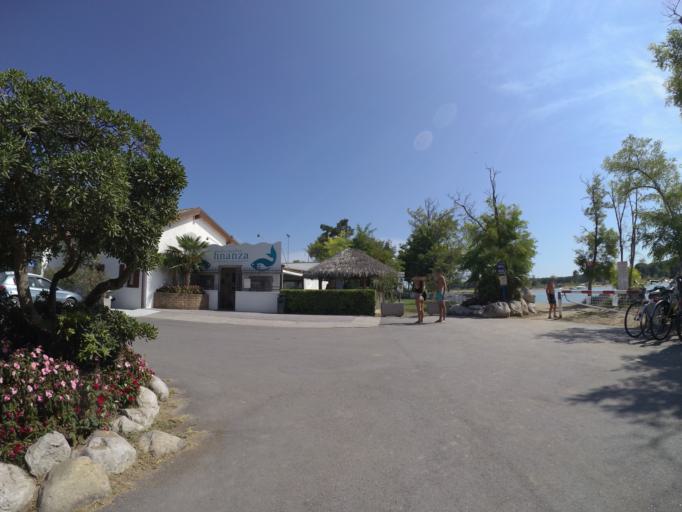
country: IT
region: Friuli Venezia Giulia
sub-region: Provincia di Udine
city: Lignano Sabbiadoro
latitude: 45.6475
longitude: 13.0971
